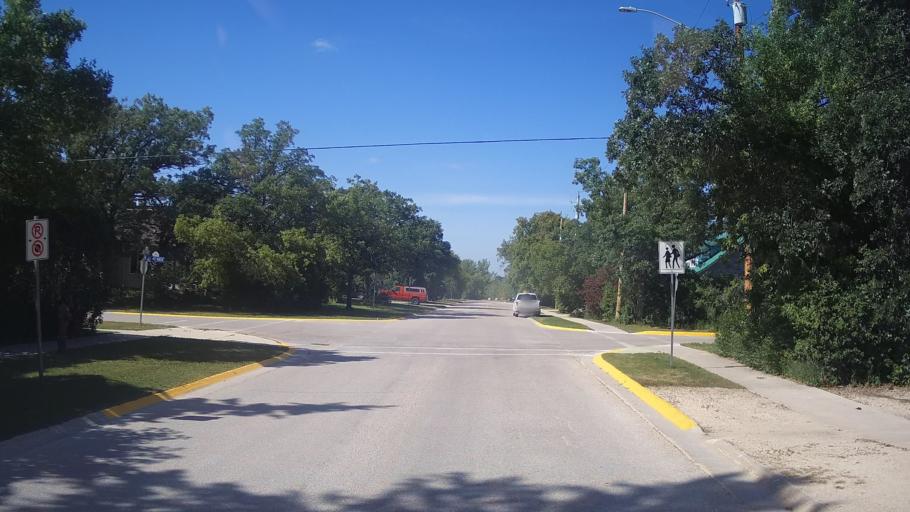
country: CA
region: Manitoba
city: Stonewall
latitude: 50.1388
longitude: -97.3266
